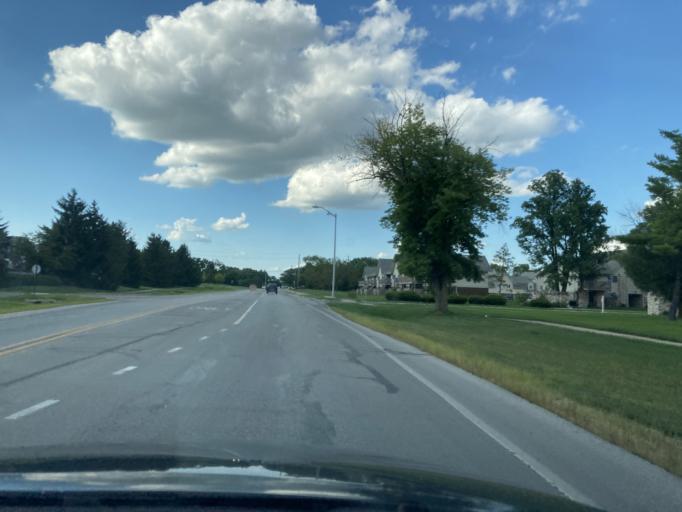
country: US
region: Indiana
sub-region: Marion County
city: Speedway
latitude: 39.8730
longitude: -86.2444
